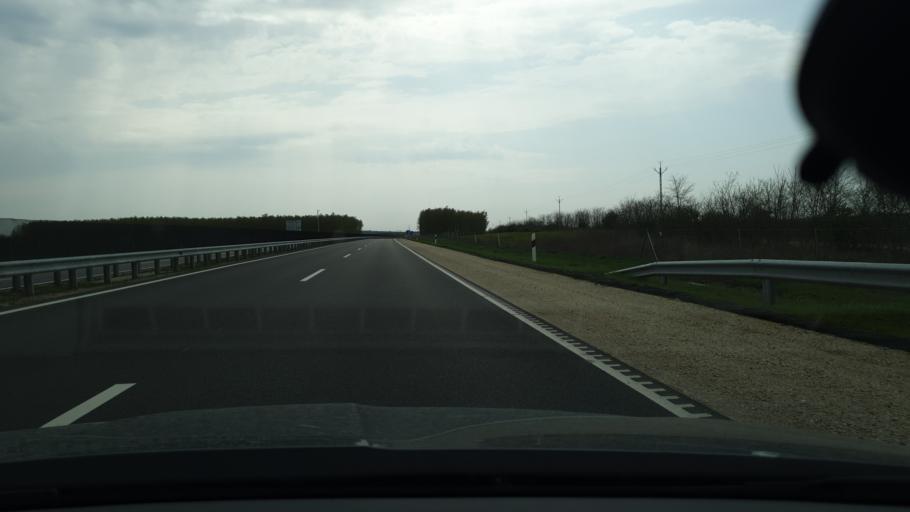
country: HU
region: Pest
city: Pilis
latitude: 47.3169
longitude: 19.5467
